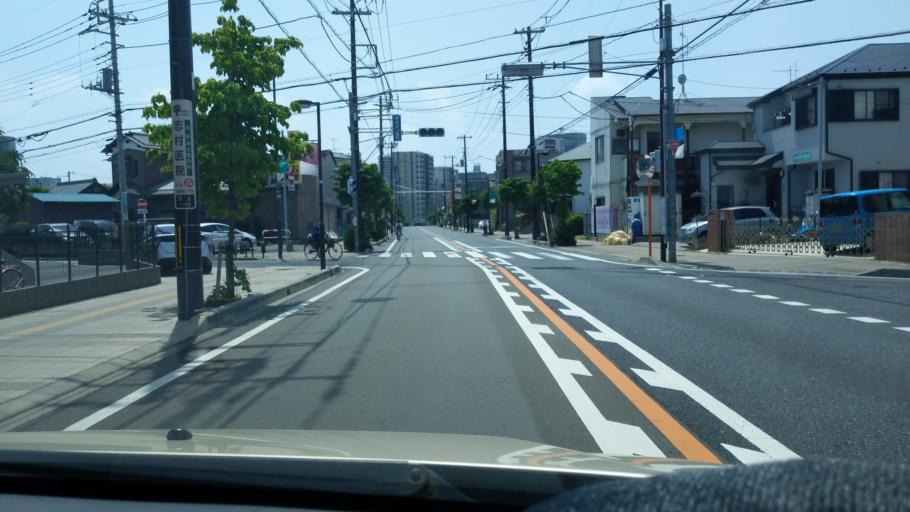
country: JP
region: Saitama
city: Yono
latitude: 35.8648
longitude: 139.6603
